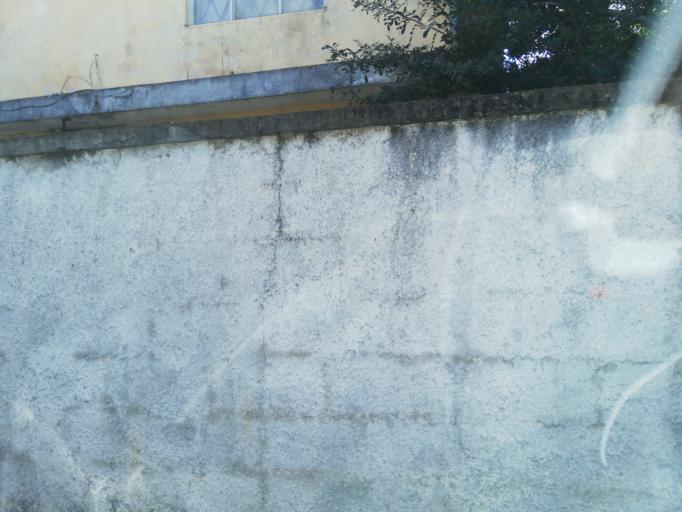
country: MU
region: Plaines Wilhems
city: Ebene
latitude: -20.2331
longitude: 57.4735
